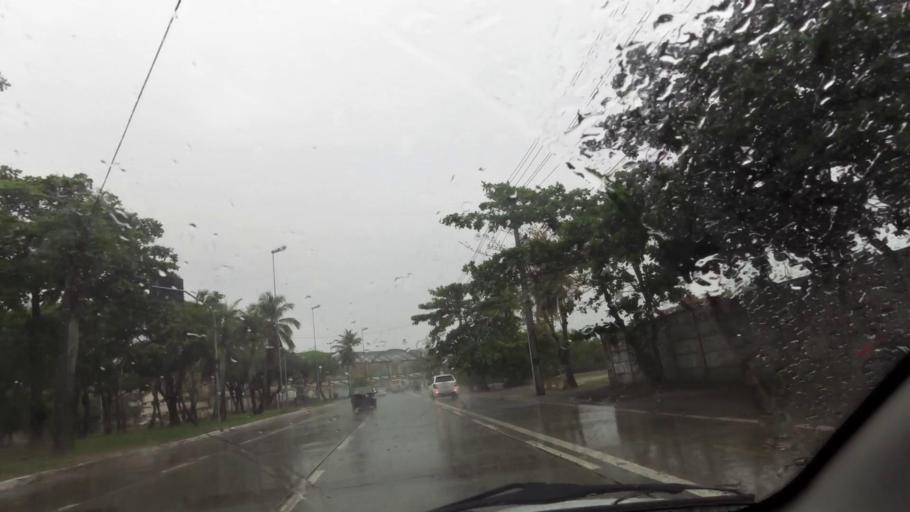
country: BR
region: Pernambuco
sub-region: Recife
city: Recife
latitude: -8.0782
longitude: -34.8913
